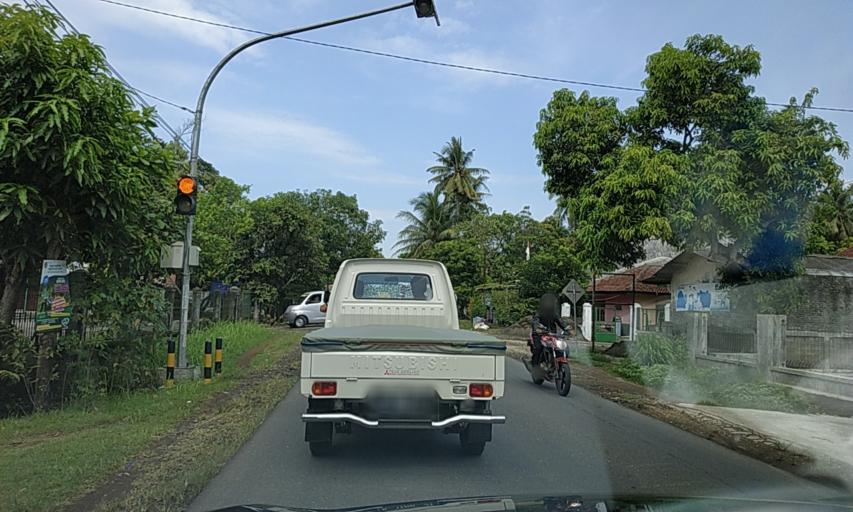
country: ID
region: Central Java
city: Mulyosari
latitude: -7.4993
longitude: 108.7879
